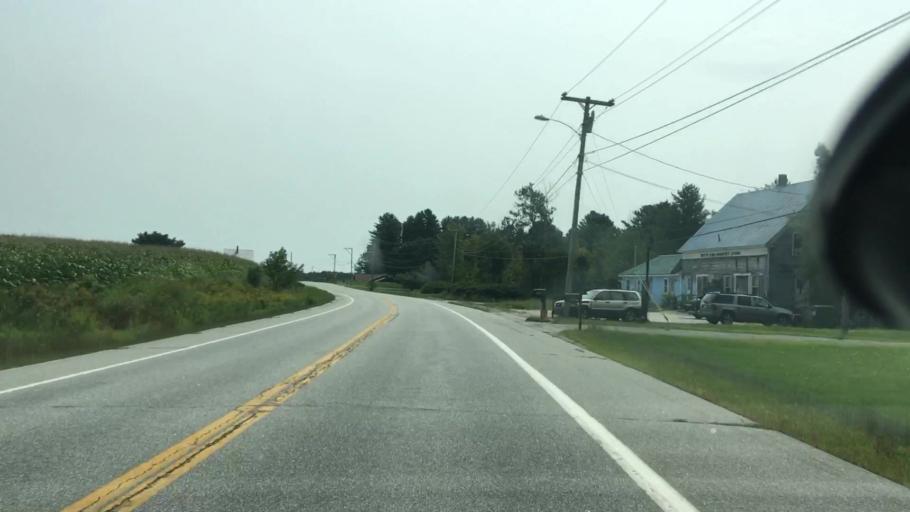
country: US
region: Maine
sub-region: Androscoggin County
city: Livermore Falls
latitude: 44.4132
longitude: -70.1436
